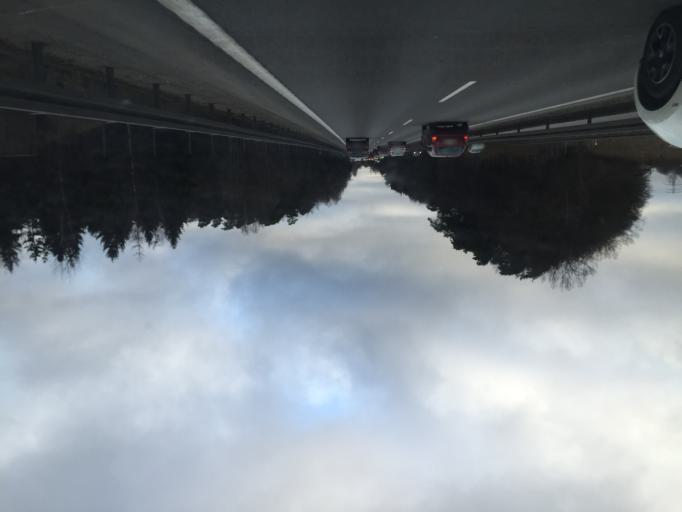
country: PL
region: Pomeranian Voivodeship
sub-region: Gdynia
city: Wielki Kack
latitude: 54.3880
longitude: 18.4979
